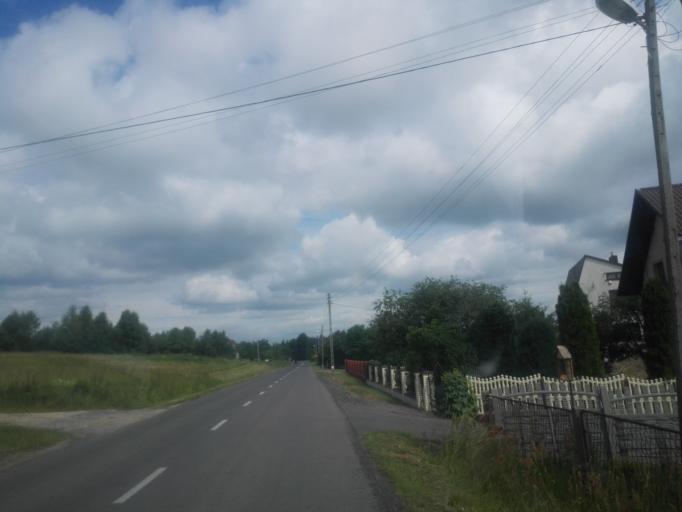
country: PL
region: Silesian Voivodeship
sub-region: Powiat czestochowski
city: Olsztyn
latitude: 50.7164
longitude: 19.3356
